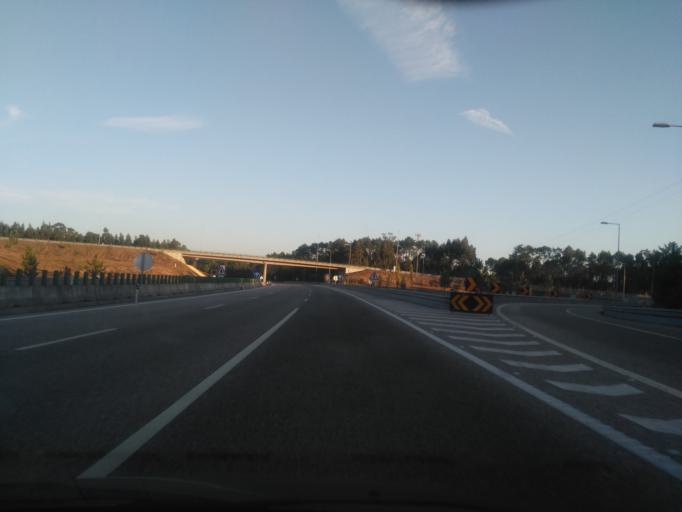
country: PT
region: Leiria
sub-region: Pombal
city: Lourical
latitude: 39.9909
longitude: -8.7967
